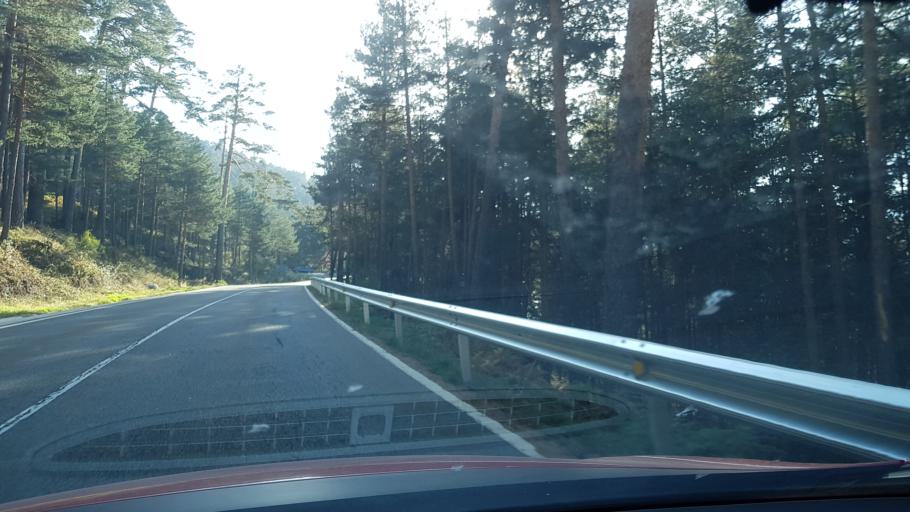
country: ES
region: Madrid
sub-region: Provincia de Madrid
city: Cercedilla
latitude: 40.8147
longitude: -4.0177
